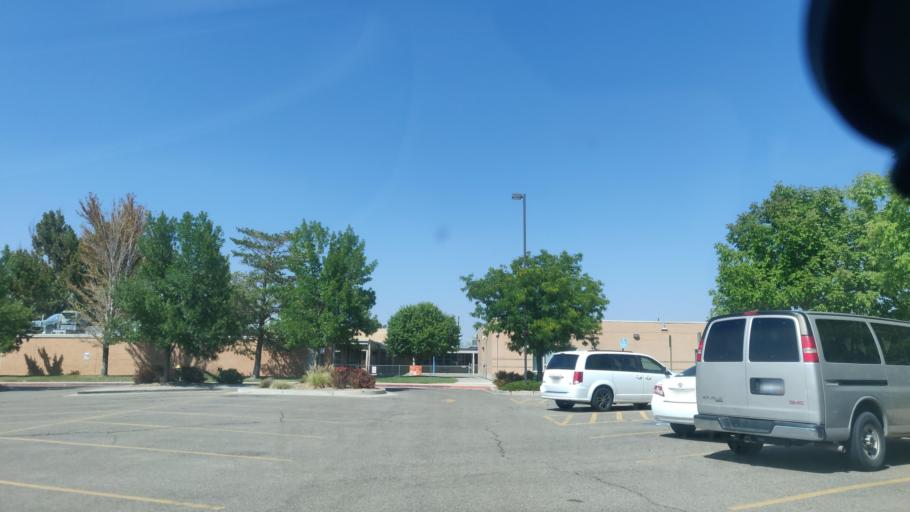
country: US
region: Colorado
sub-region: Mesa County
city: Grand Junction
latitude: 39.0898
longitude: -108.5793
